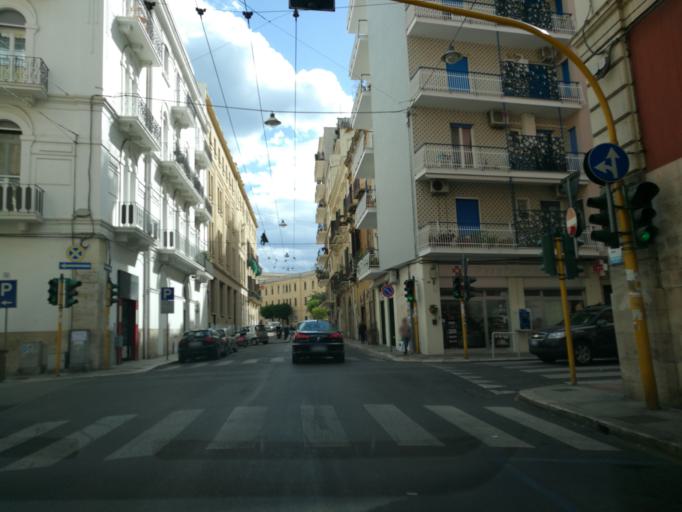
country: IT
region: Apulia
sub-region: Provincia di Bari
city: Bari
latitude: 41.1268
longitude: 16.8625
